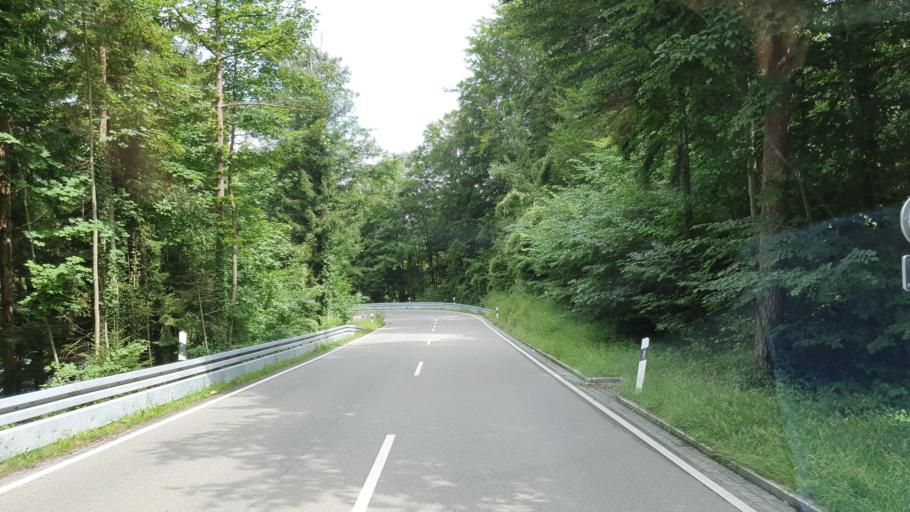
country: AT
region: Vorarlberg
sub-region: Politischer Bezirk Bregenz
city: Moggers
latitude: 47.5933
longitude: 9.8162
